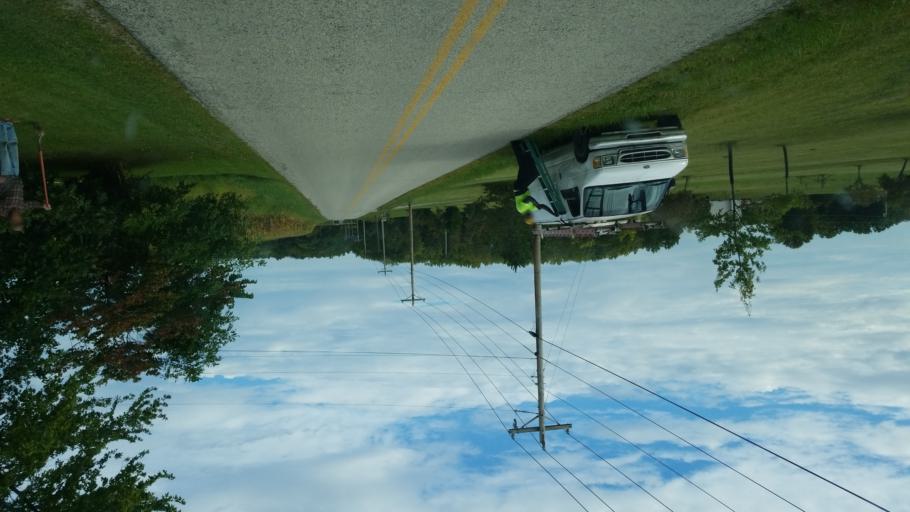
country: US
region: Ohio
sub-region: Knox County
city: Centerburg
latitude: 40.3163
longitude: -82.7714
